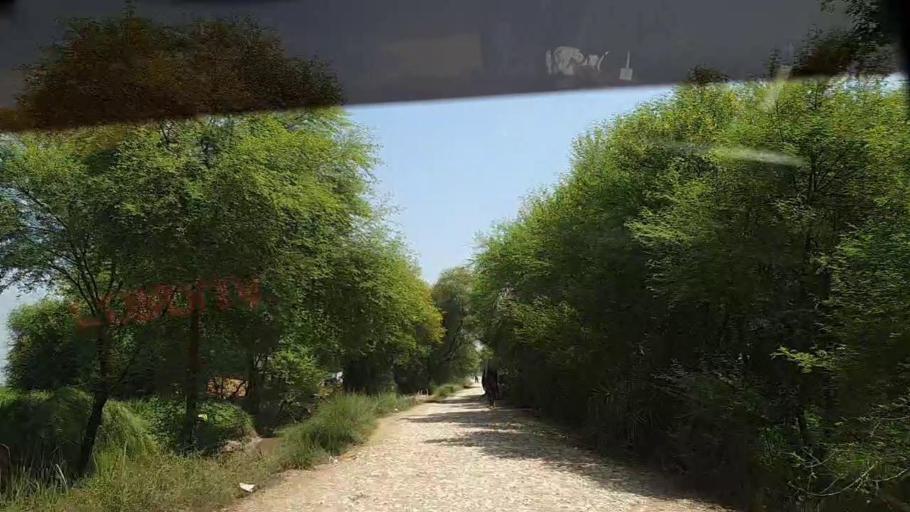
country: PK
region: Sindh
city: Ghauspur
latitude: 28.1715
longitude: 69.0612
